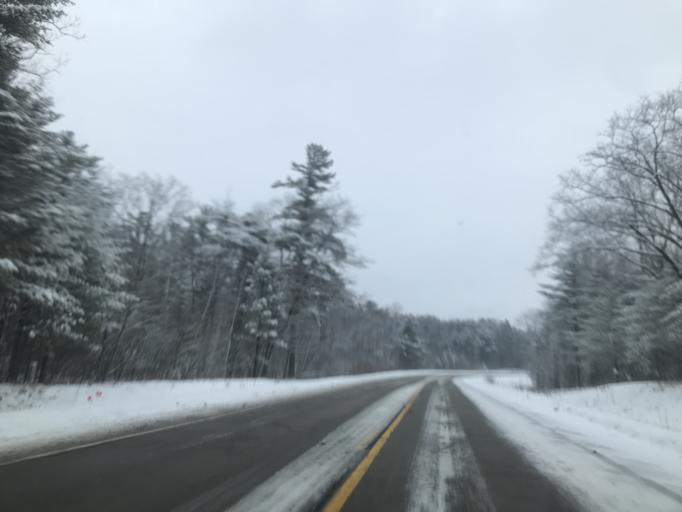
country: US
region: Wisconsin
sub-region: Oconto County
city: Oconto Falls
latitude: 44.8616
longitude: -88.0938
